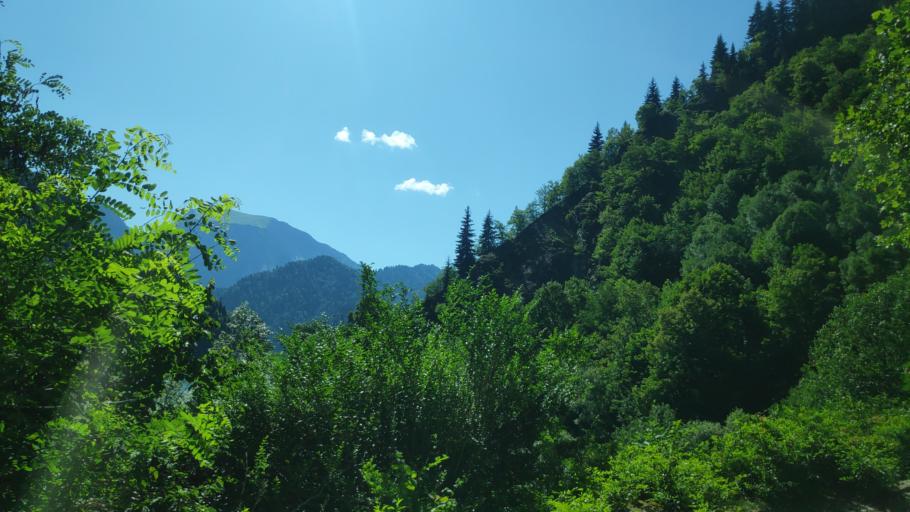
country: GE
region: Abkhazia
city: Gagra
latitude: 43.4831
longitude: 40.5594
